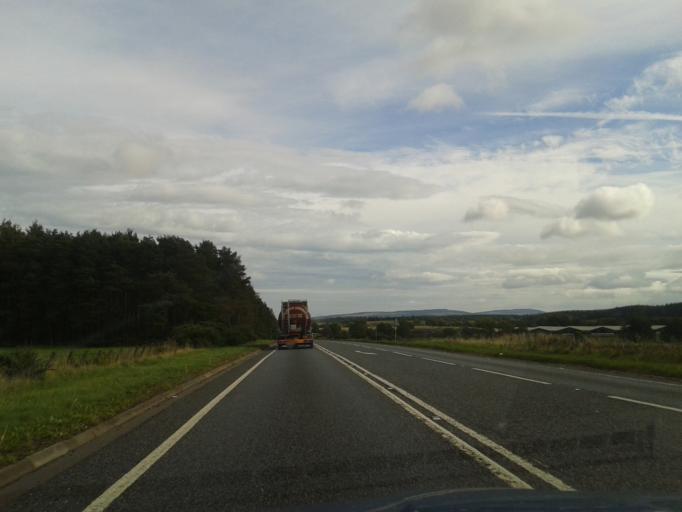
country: GB
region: Scotland
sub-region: Moray
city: Forres
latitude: 57.5860
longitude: -3.7391
